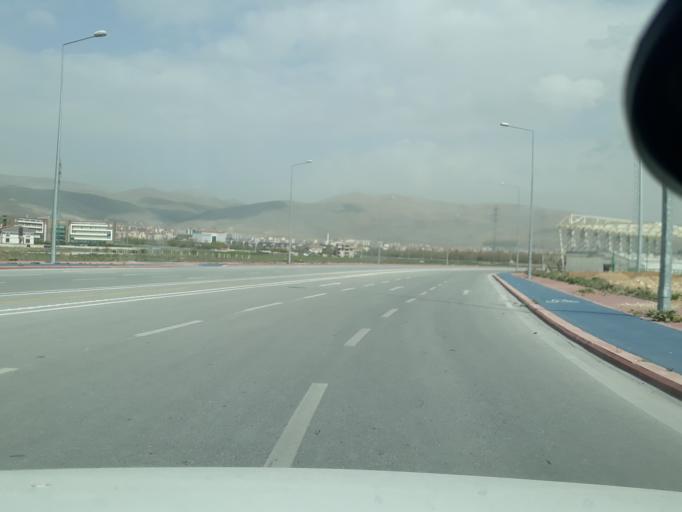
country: TR
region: Konya
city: Selcuklu
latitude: 37.9428
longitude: 32.4814
